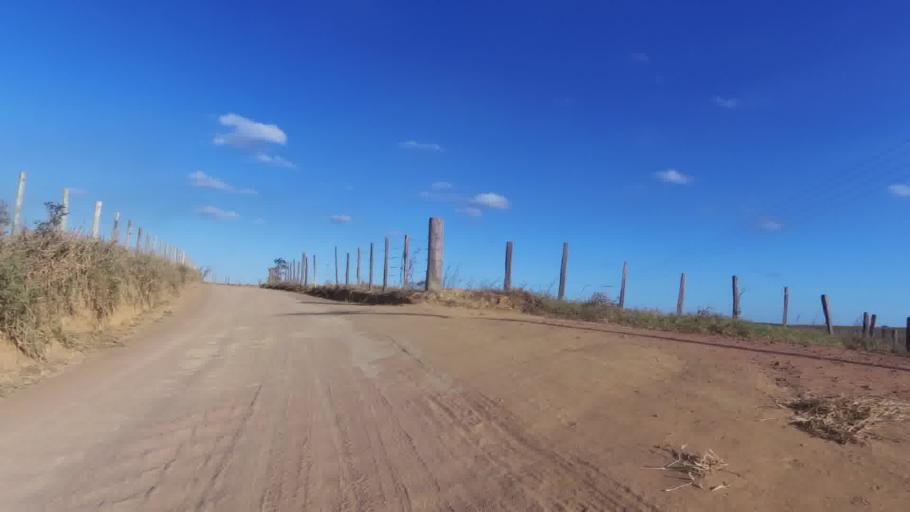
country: BR
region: Espirito Santo
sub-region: Marataizes
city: Marataizes
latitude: -21.1516
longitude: -41.0646
